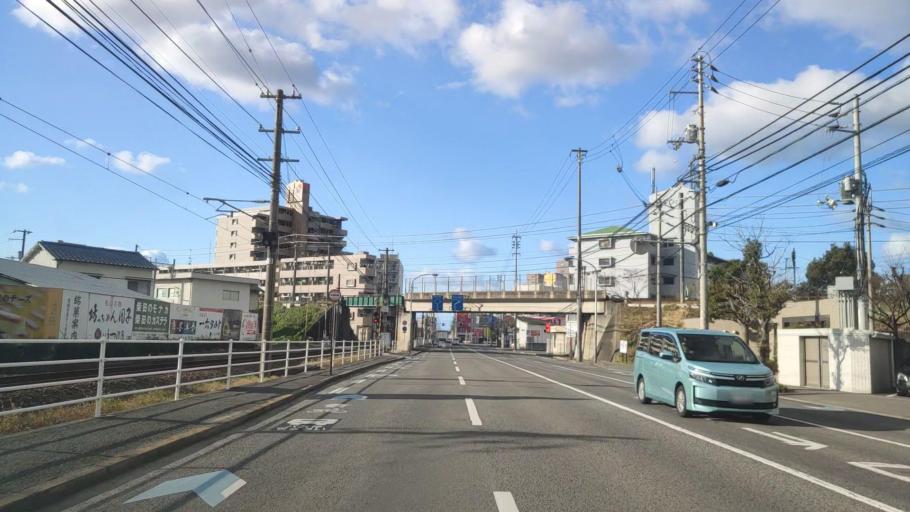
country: JP
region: Ehime
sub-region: Shikoku-chuo Shi
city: Matsuyama
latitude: 33.8300
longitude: 132.7523
